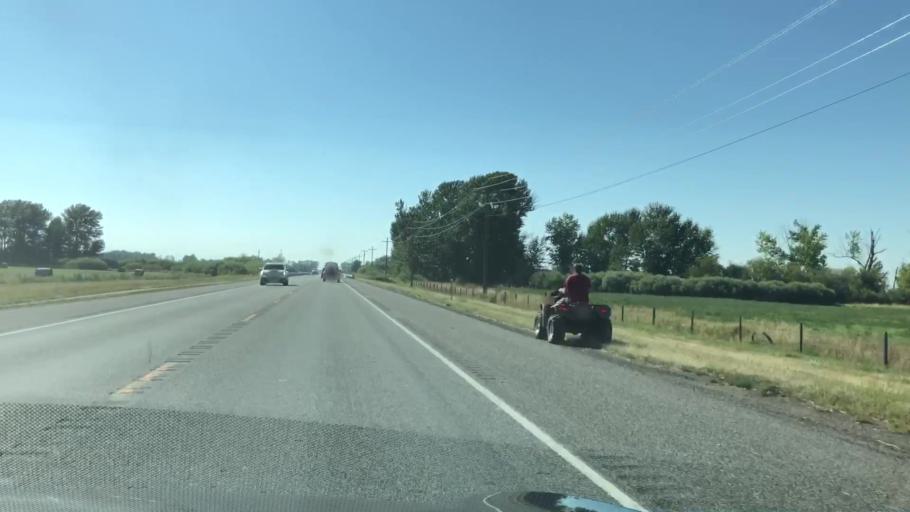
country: US
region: Montana
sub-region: Gallatin County
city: Belgrade
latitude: 45.7292
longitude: -111.1519
